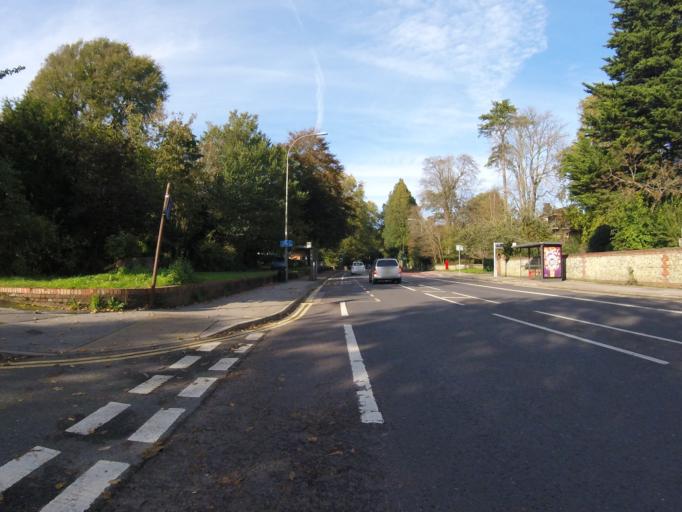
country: GB
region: England
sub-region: Brighton and Hove
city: Hove
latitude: 50.8477
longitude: -0.1525
